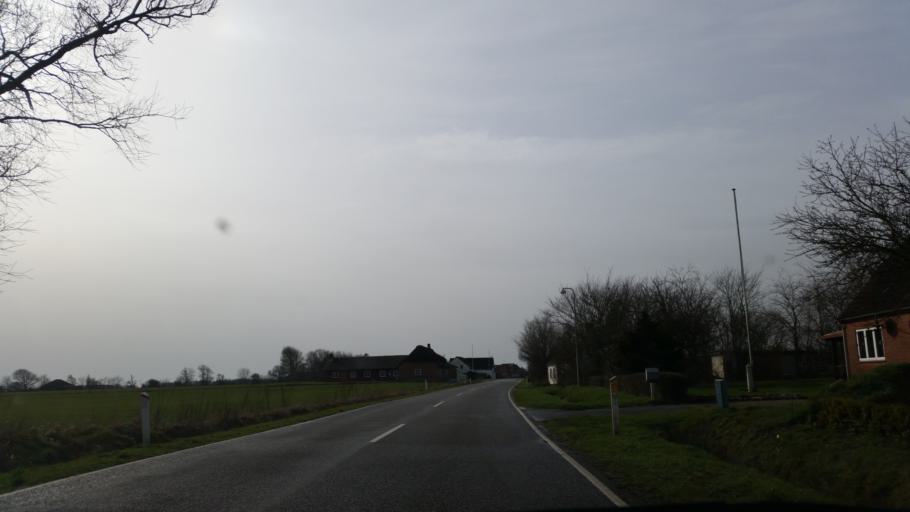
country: DK
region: South Denmark
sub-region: Tonder Kommune
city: Sherrebek
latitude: 55.0779
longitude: 8.6798
